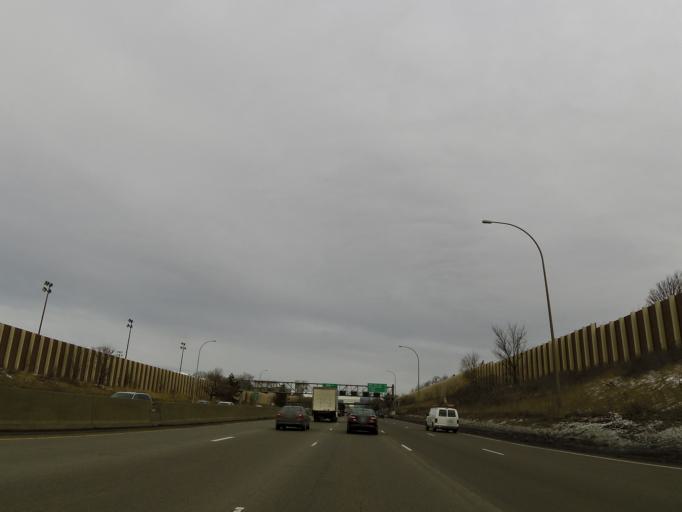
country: US
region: Minnesota
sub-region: Hennepin County
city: Richfield
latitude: 44.9277
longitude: -93.2745
